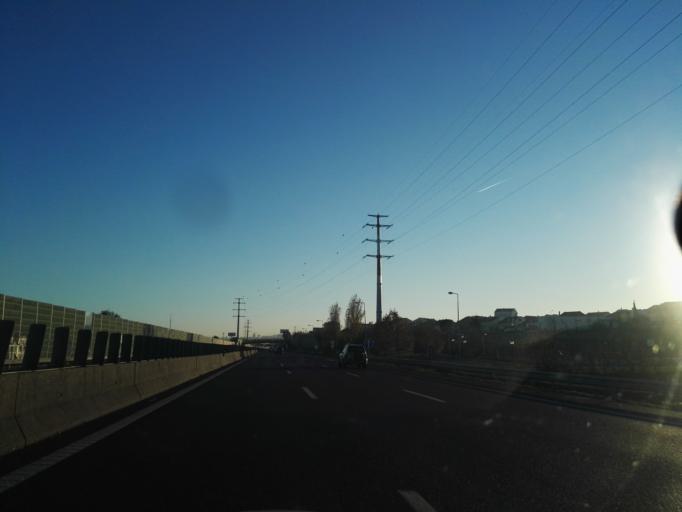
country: PT
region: Lisbon
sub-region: Loures
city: Sao Joao da Talha
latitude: 38.8233
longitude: -9.0992
